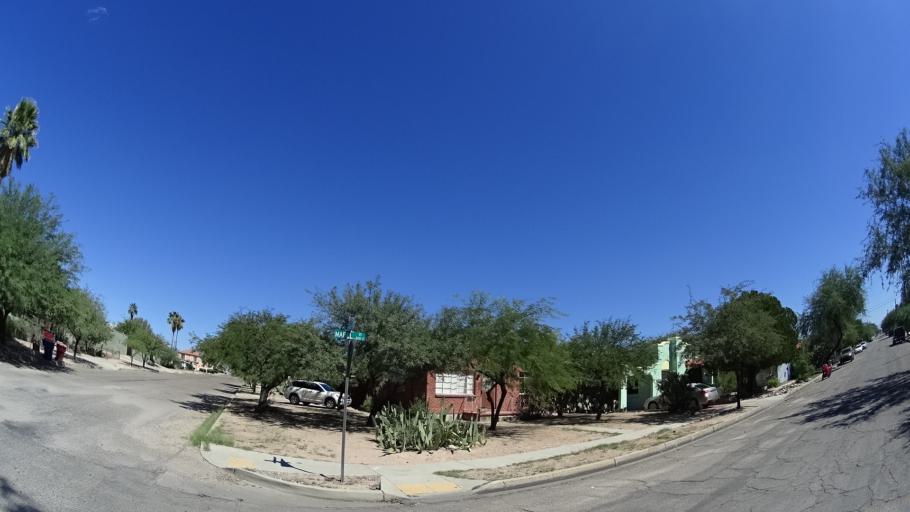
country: US
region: Arizona
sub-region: Pima County
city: South Tucson
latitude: 32.2385
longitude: -110.9641
